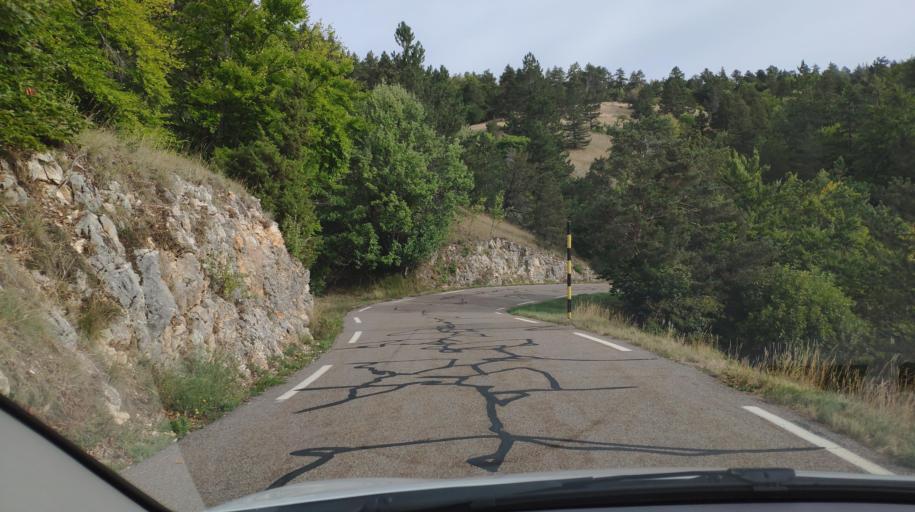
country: FR
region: Provence-Alpes-Cote d'Azur
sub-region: Departement du Vaucluse
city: Sault
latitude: 44.1572
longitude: 5.3475
